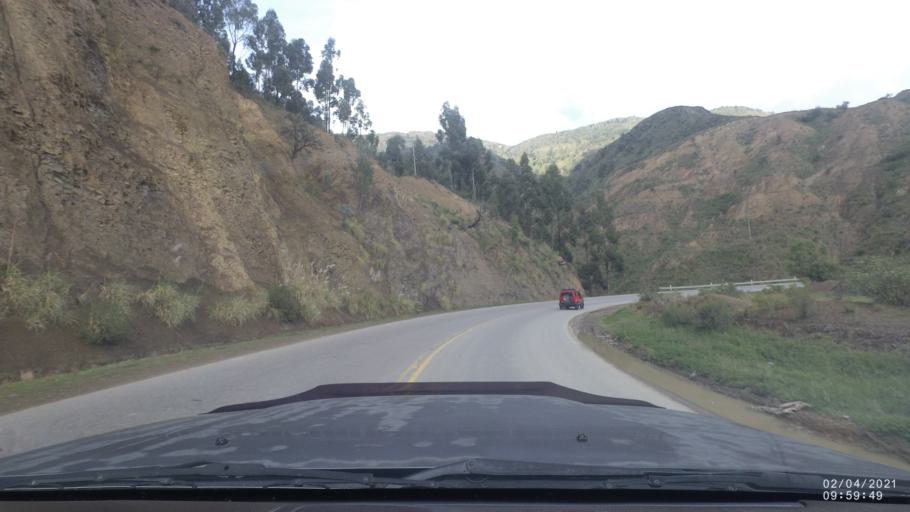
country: BO
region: Cochabamba
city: Irpa Irpa
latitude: -17.6796
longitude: -66.4242
